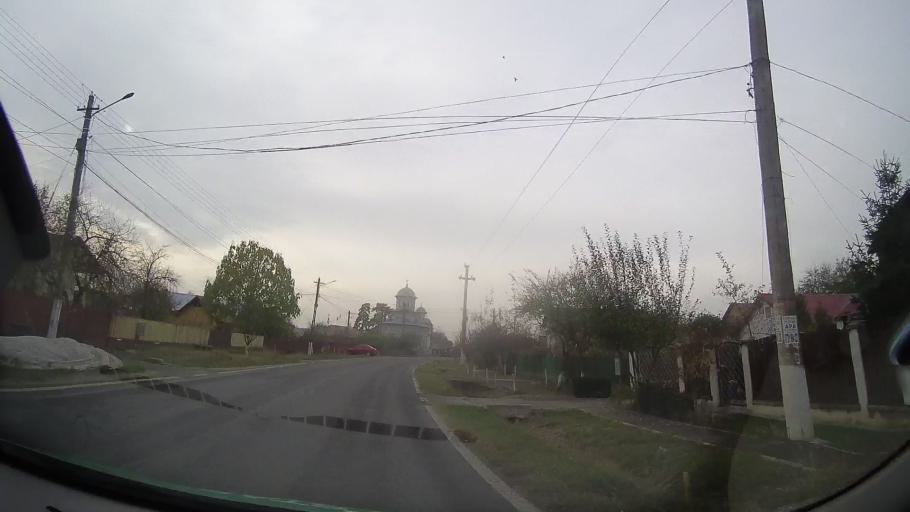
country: RO
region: Ilfov
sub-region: Comuna Gruiu
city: Silistea Snagovului
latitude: 44.7448
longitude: 26.1801
